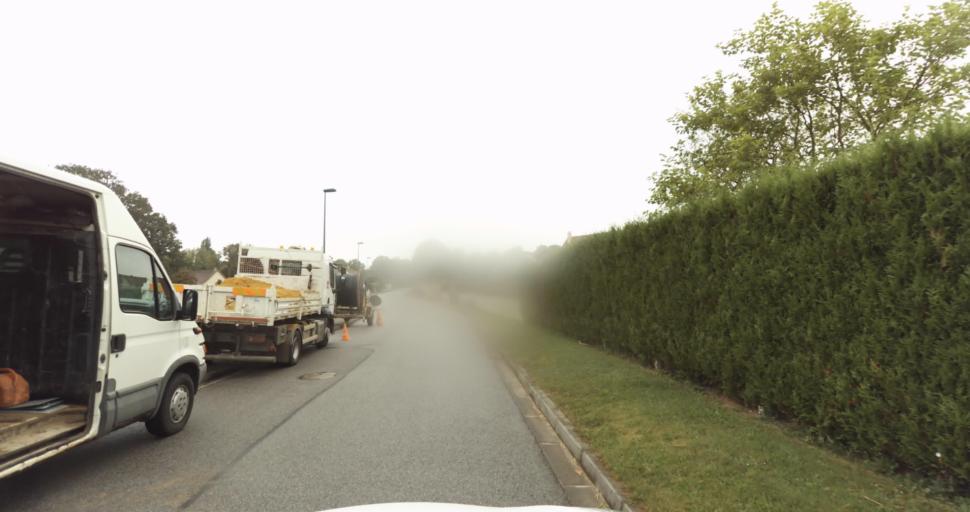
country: FR
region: Haute-Normandie
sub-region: Departement de l'Eure
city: Normanville
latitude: 49.0975
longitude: 1.1488
